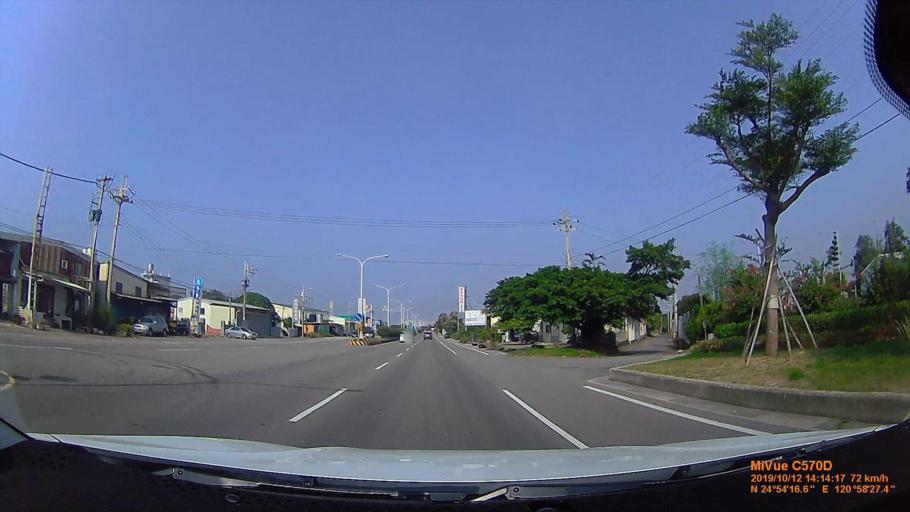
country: TW
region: Taiwan
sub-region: Hsinchu
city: Zhubei
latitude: 24.9085
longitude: 120.9775
